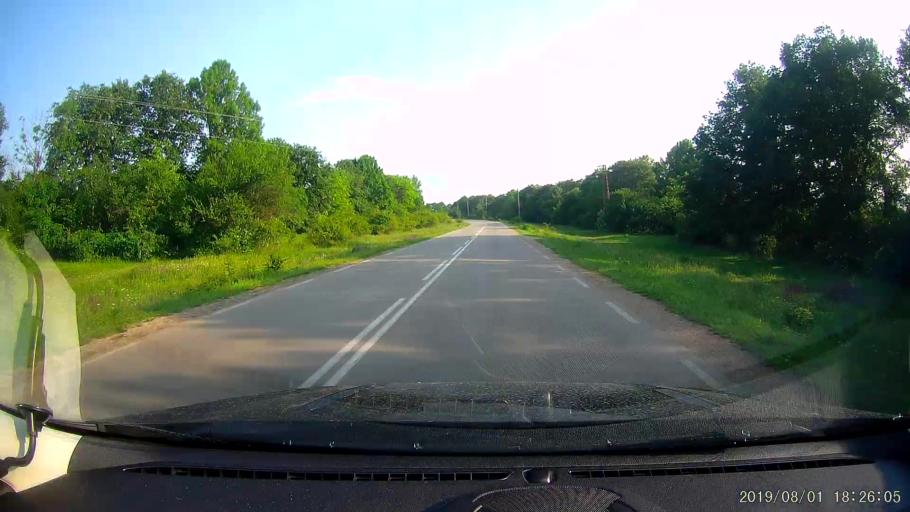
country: BG
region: Shumen
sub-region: Obshtina Venets
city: Venets
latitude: 43.6073
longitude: 26.9947
